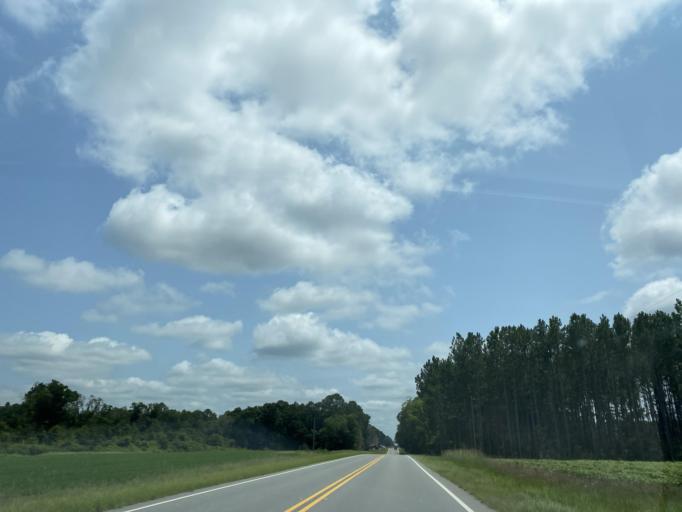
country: US
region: Georgia
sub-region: Jeff Davis County
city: Hazlehurst
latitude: 31.7164
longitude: -82.5226
